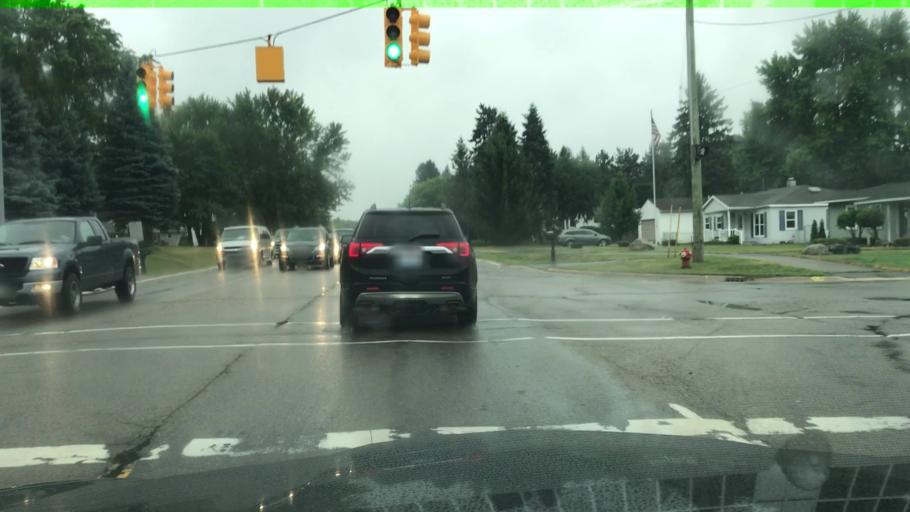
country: US
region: Michigan
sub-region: Oakland County
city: Auburn Hills
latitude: 42.7276
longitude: -83.2874
